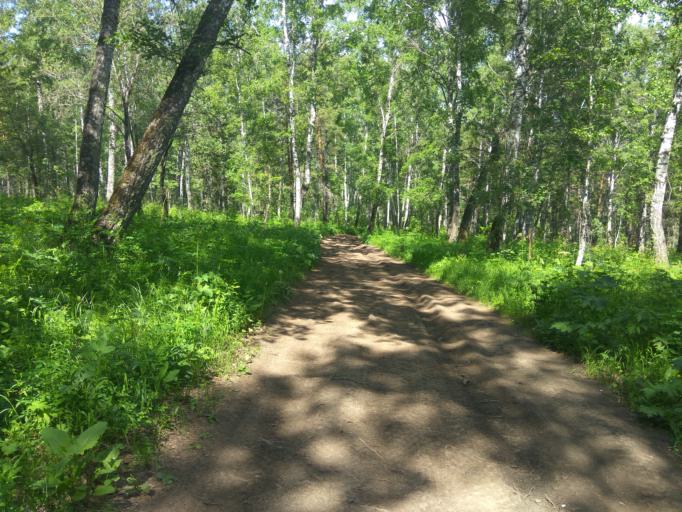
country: RU
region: Krasnoyarskiy
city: Krasnoyarsk
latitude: 55.9502
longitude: 92.8685
